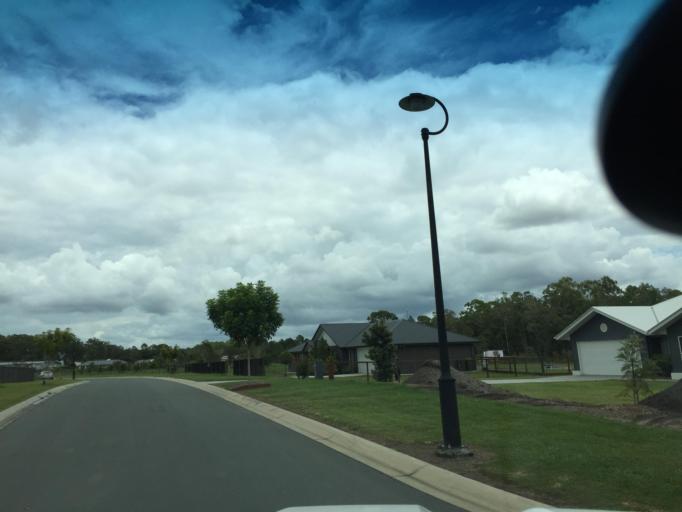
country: AU
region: Queensland
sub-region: Moreton Bay
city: Caboolture
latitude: -27.0413
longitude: 152.9300
